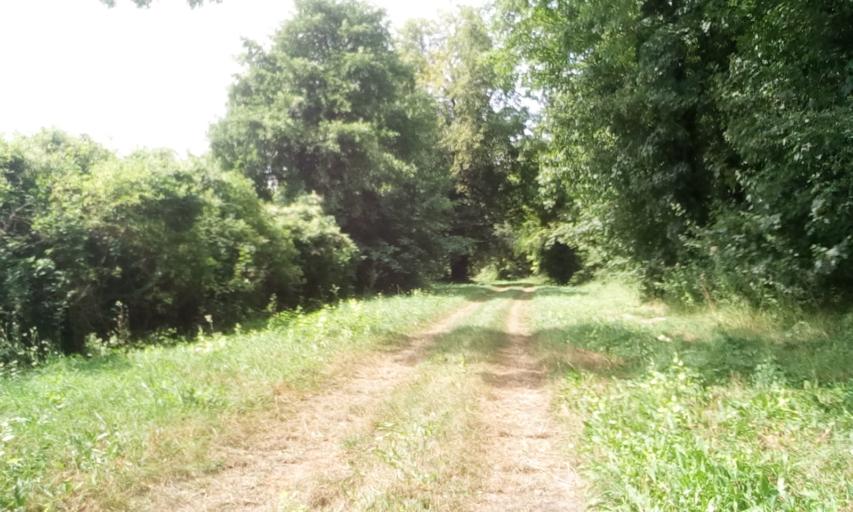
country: FR
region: Lower Normandy
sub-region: Departement du Calvados
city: Sannerville
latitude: 49.1587
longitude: -0.2099
